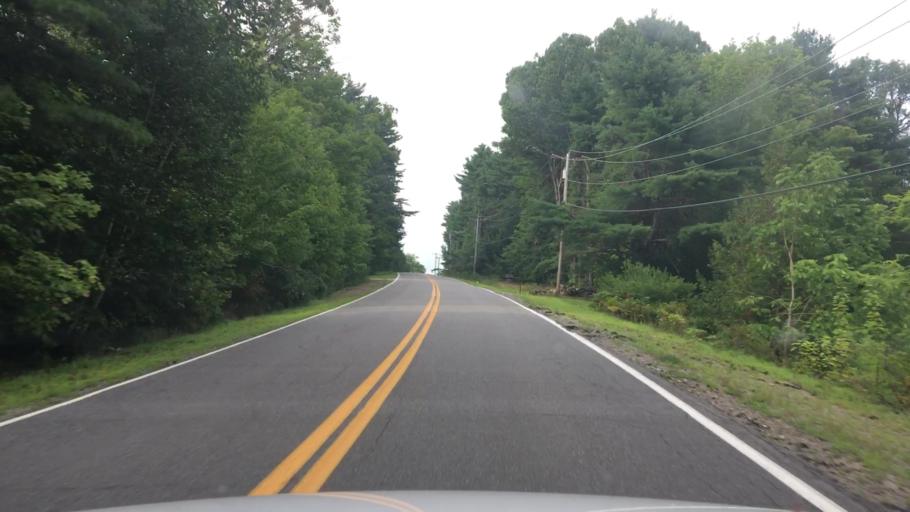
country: US
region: Maine
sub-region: Knox County
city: Washington
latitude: 44.2618
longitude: -69.3738
